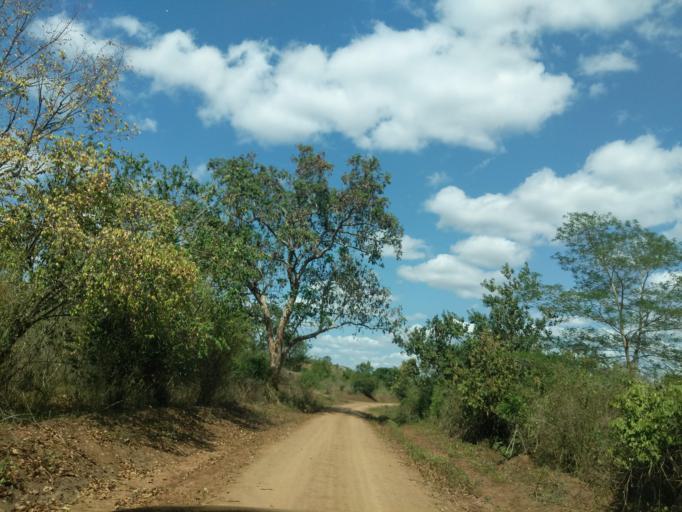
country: TZ
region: Tanga
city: Chanika
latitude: -5.5083
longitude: 38.3660
